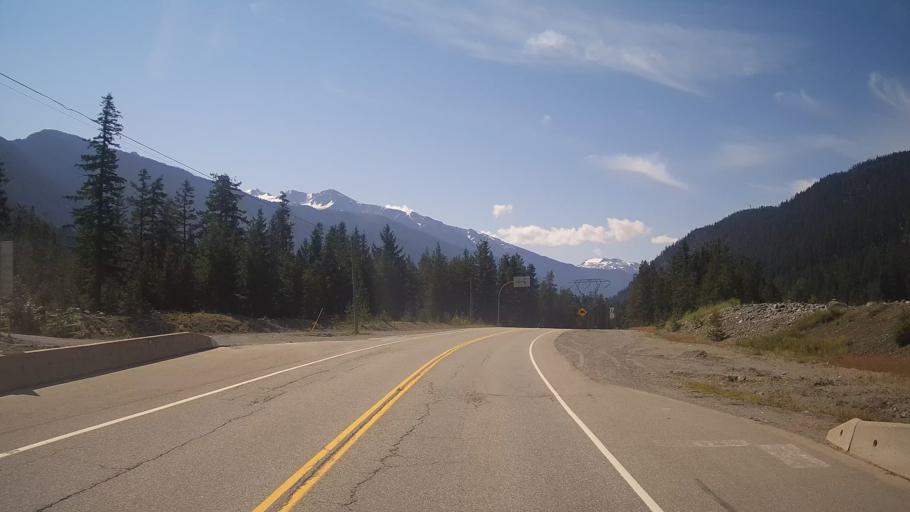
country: CA
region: British Columbia
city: Pemberton
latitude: 50.2713
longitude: -122.8673
